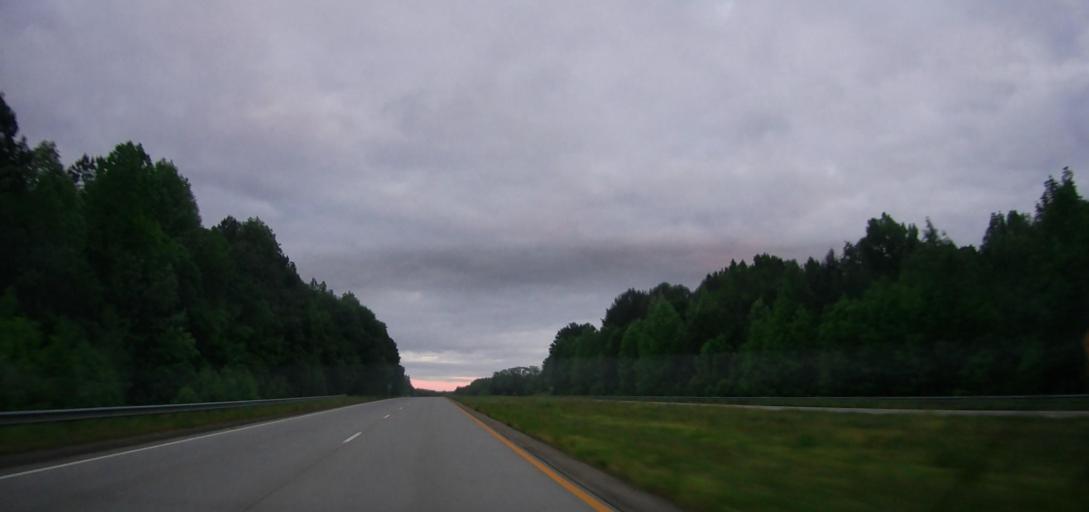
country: US
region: Georgia
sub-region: Jackson County
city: Jefferson
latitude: 34.0941
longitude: -83.5861
